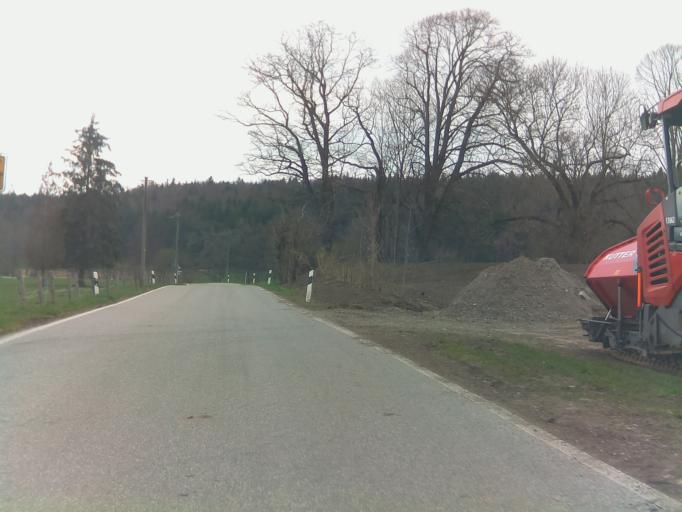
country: DE
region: Bavaria
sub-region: Upper Bavaria
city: Obersochering
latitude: 47.7606
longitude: 11.2288
